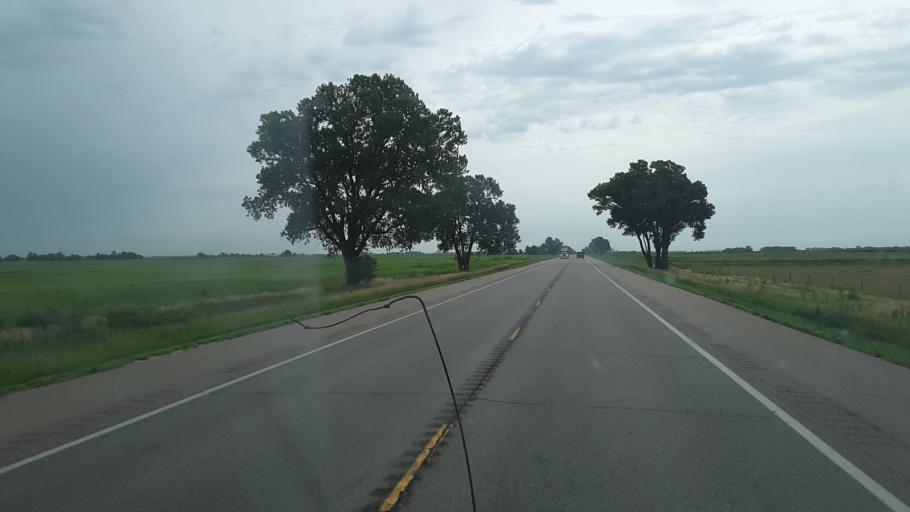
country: US
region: Kansas
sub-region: Stafford County
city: Saint John
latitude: 37.9560
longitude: -98.7866
